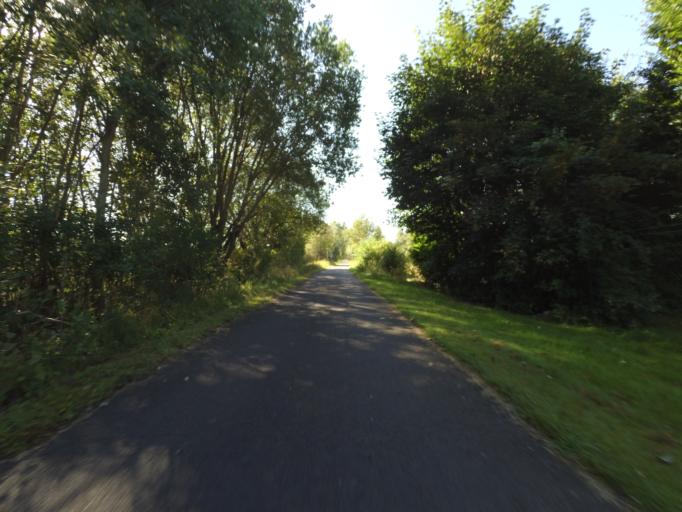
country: DE
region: Rheinland-Pfalz
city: Udler
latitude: 50.1533
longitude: 6.8769
